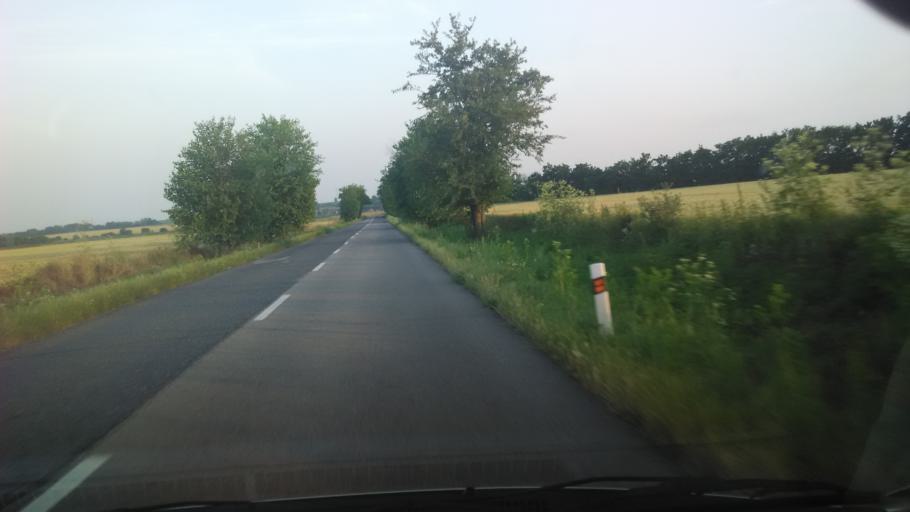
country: SK
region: Nitriansky
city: Tlmace
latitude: 48.1663
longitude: 18.4516
